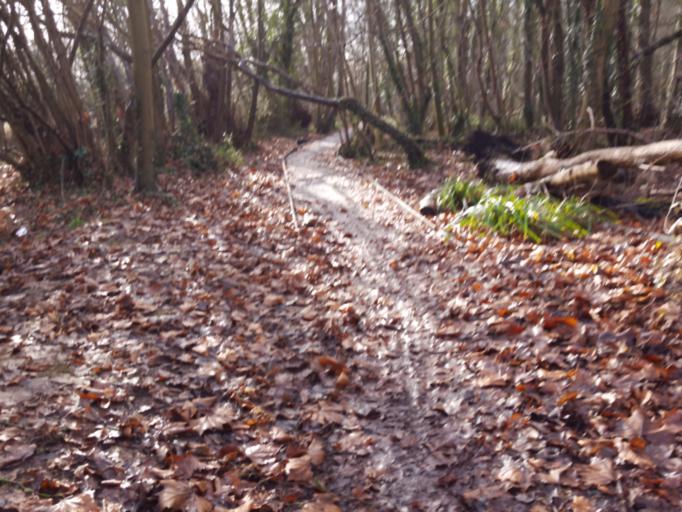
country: GB
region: England
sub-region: Essex
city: Harlow
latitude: 51.7848
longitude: 0.1017
